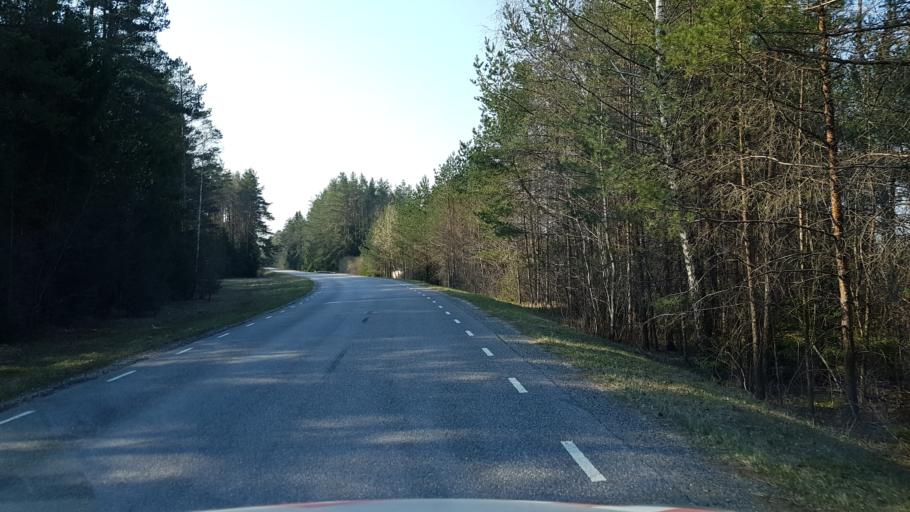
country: EE
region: Raplamaa
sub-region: Kohila vald
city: Kohila
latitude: 59.1949
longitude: 24.6636
